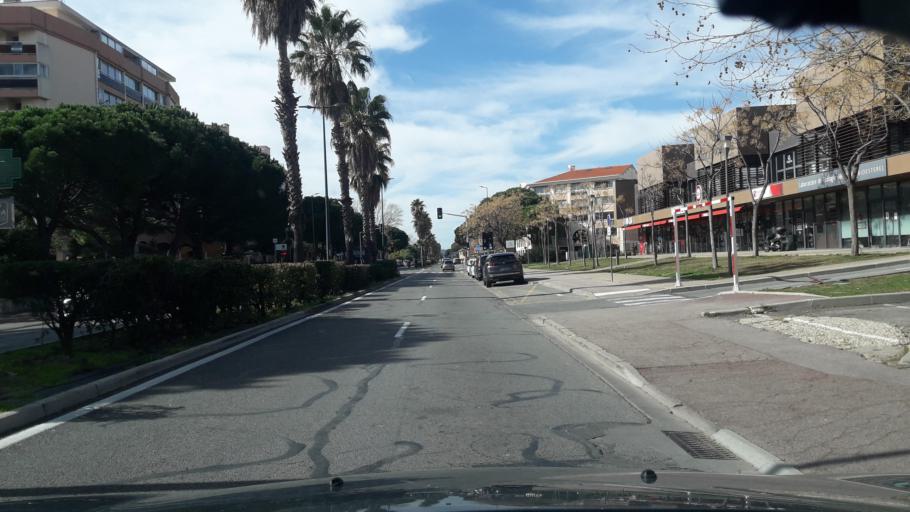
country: FR
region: Provence-Alpes-Cote d'Azur
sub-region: Departement du Var
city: Frejus
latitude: 43.4268
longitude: 6.7539
